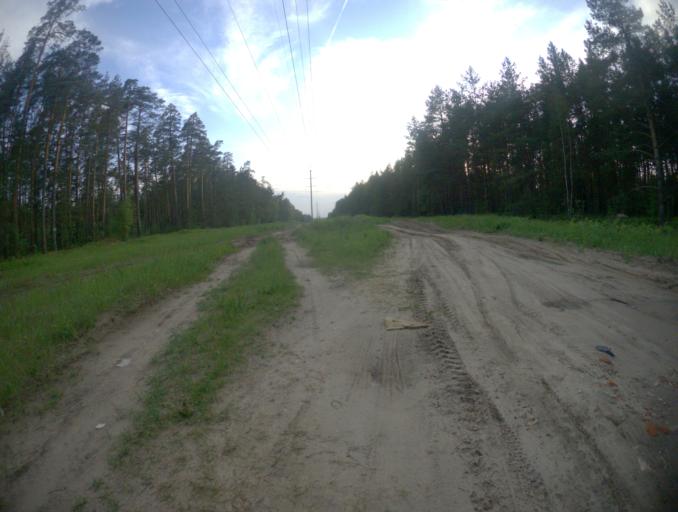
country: RU
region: Vladimir
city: Gus'-Khrustal'nyy
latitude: 55.6329
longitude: 40.6844
